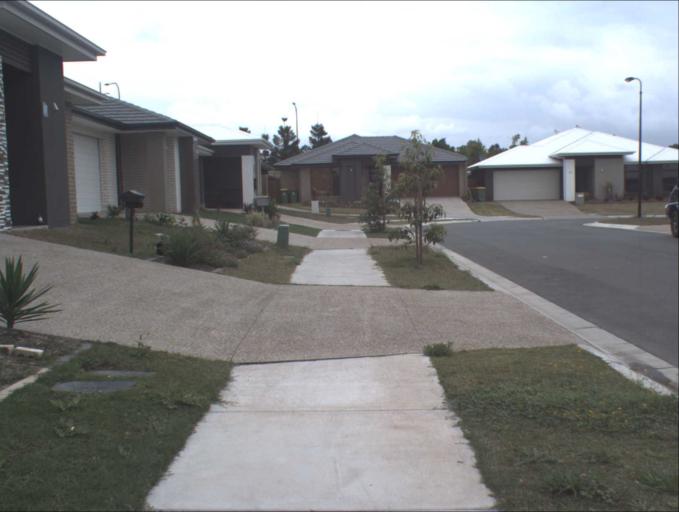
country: AU
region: Queensland
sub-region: Logan
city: Waterford West
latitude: -27.7102
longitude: 153.1160
